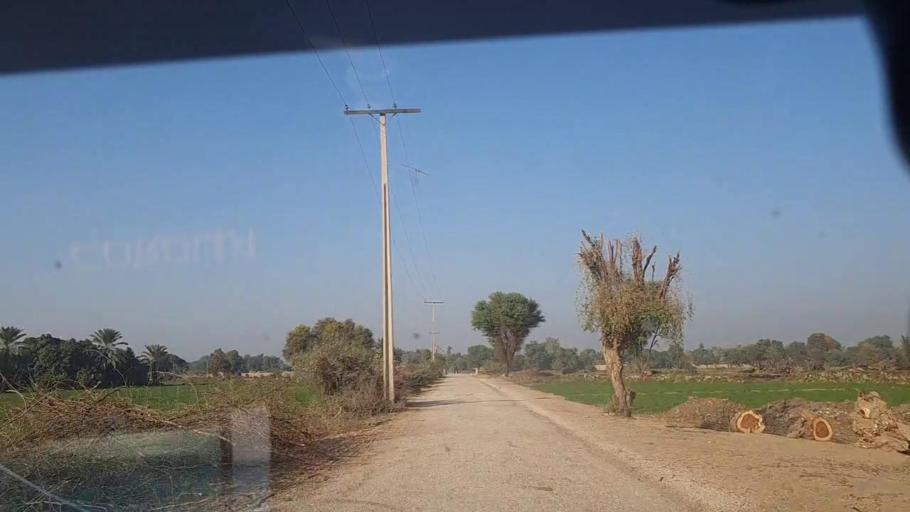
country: PK
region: Sindh
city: Sobhadero
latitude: 27.2515
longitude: 68.3503
